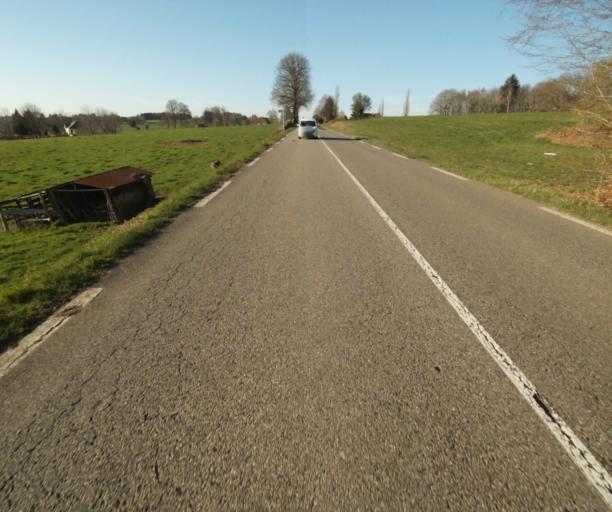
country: FR
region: Limousin
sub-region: Departement de la Correze
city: Seilhac
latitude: 45.3725
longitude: 1.7252
